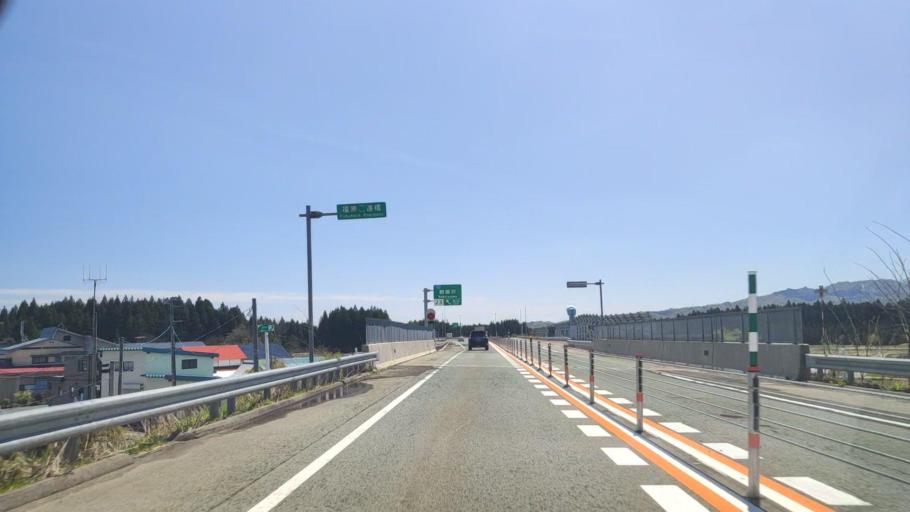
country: JP
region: Yamagata
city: Obanazawa
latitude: 38.6388
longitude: 140.3731
